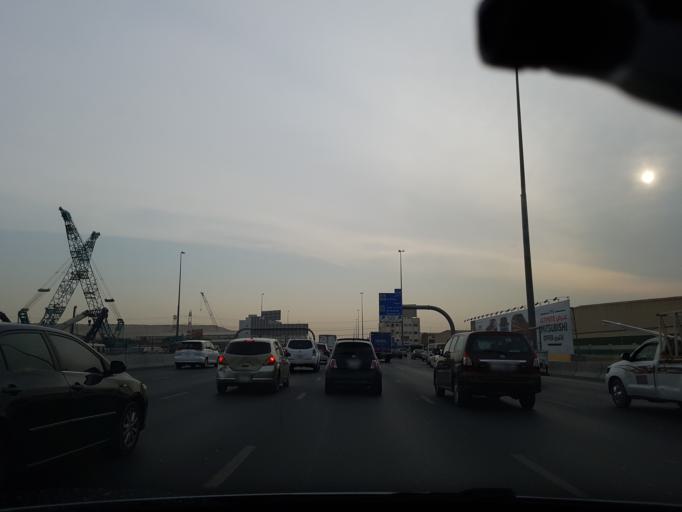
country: AE
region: Ash Shariqah
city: Sharjah
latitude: 25.2920
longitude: 55.4325
